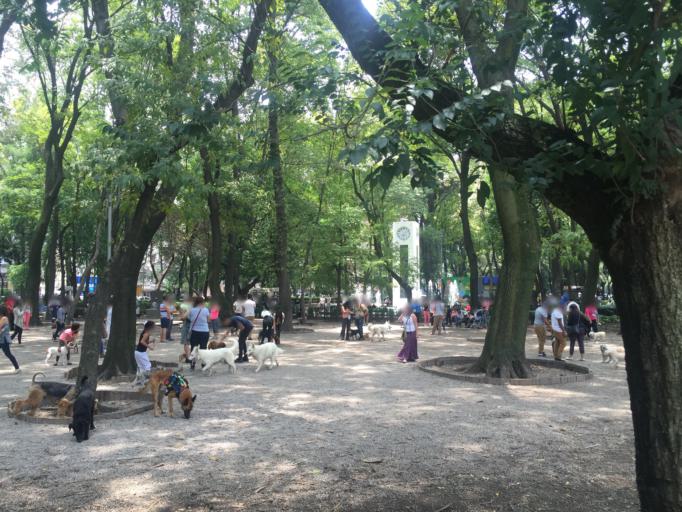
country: MX
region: Mexico City
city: Benito Juarez
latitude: 19.4113
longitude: -99.1695
